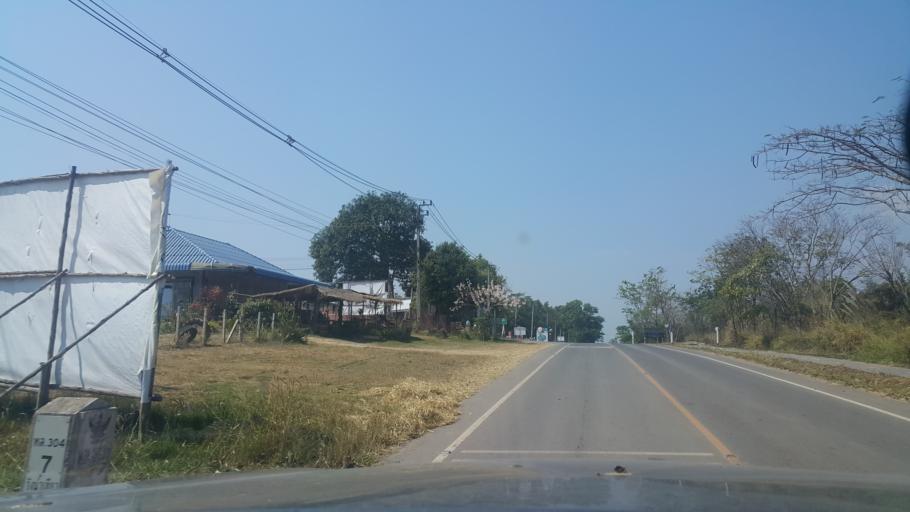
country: TH
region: Nakhon Ratchasima
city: Wang Nam Khiao
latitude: 14.3557
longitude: 101.9268
